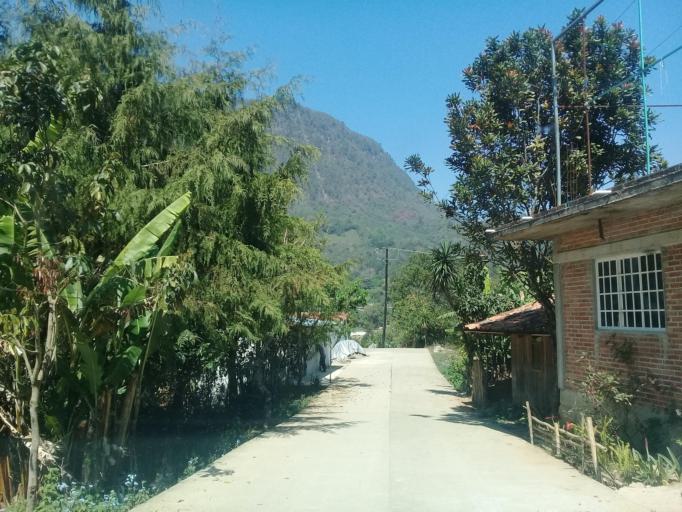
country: MX
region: Veracruz
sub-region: Tlilapan
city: Tonalixco
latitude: 18.7569
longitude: -97.0430
